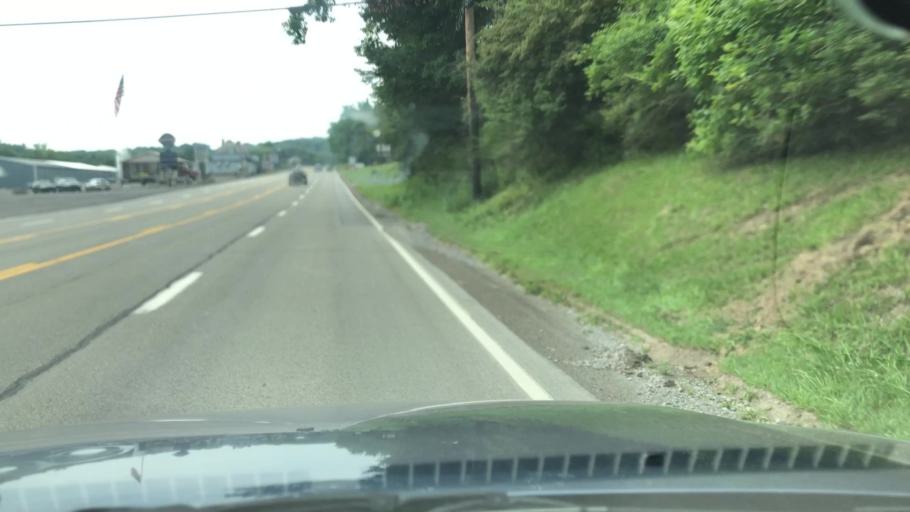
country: US
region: Pennsylvania
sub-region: Allegheny County
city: Bakerstown
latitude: 40.6767
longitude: -79.9336
